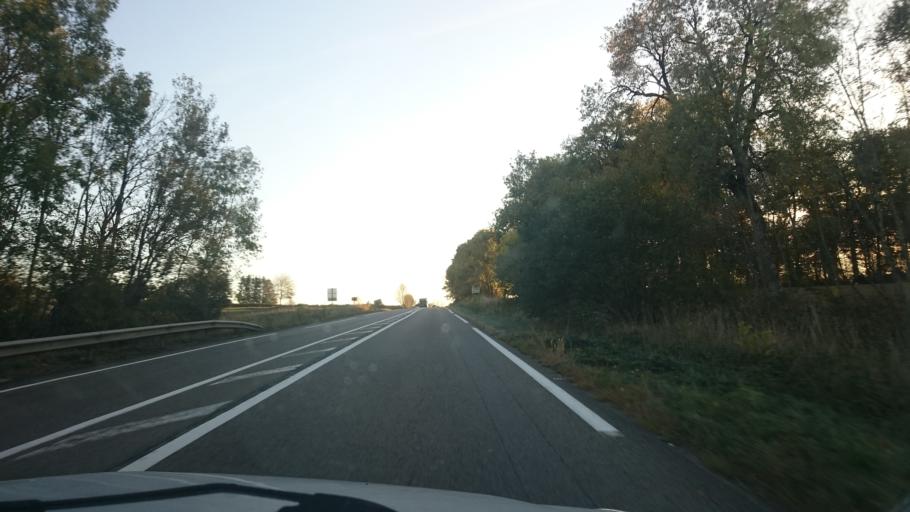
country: FR
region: Franche-Comte
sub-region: Departement du Doubs
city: Quingey
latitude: 47.0572
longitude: 5.8814
